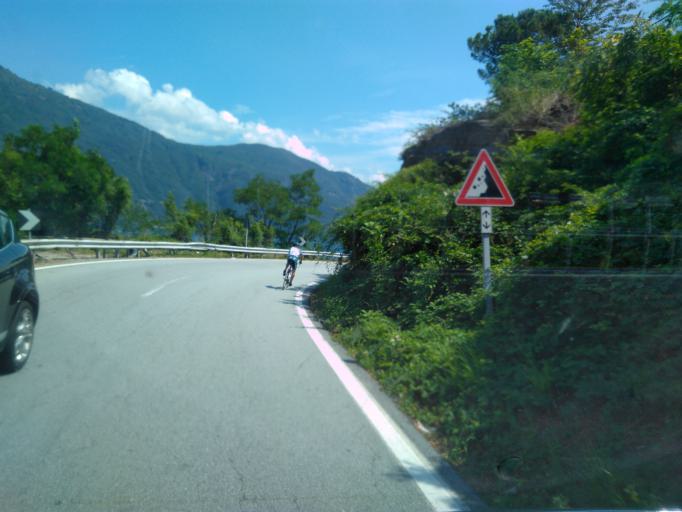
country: IT
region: Piedmont
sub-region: Provincia Verbano-Cusio-Ossola
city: Cannobio
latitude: 46.0765
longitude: 8.6946
